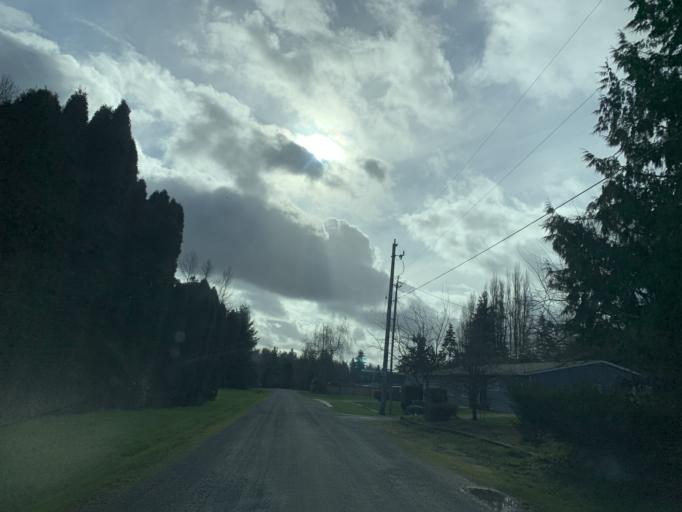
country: US
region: Washington
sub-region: Pierce County
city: Edgewood
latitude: 47.2350
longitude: -122.3000
